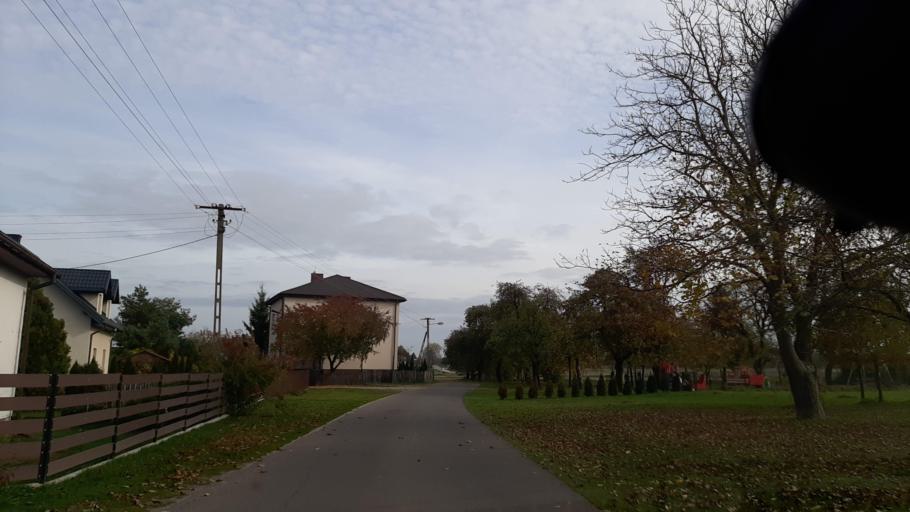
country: PL
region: Lublin Voivodeship
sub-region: Powiat lubelski
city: Garbow
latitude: 51.4097
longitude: 22.3887
